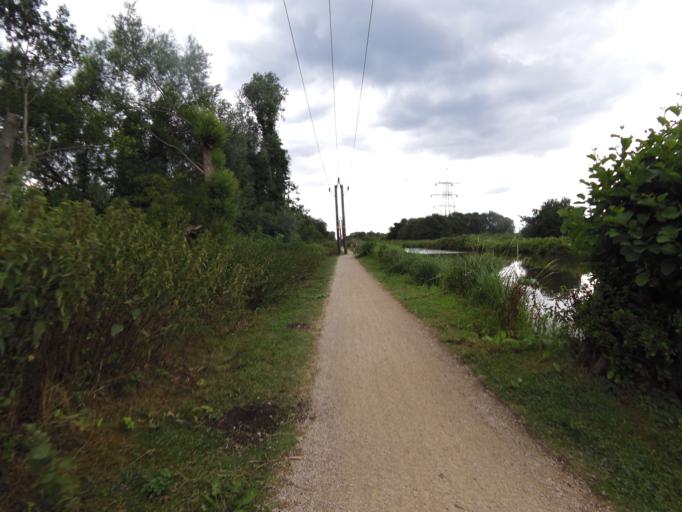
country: GB
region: England
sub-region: Hertfordshire
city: Cheshunt
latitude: 51.7178
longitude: -0.0151
